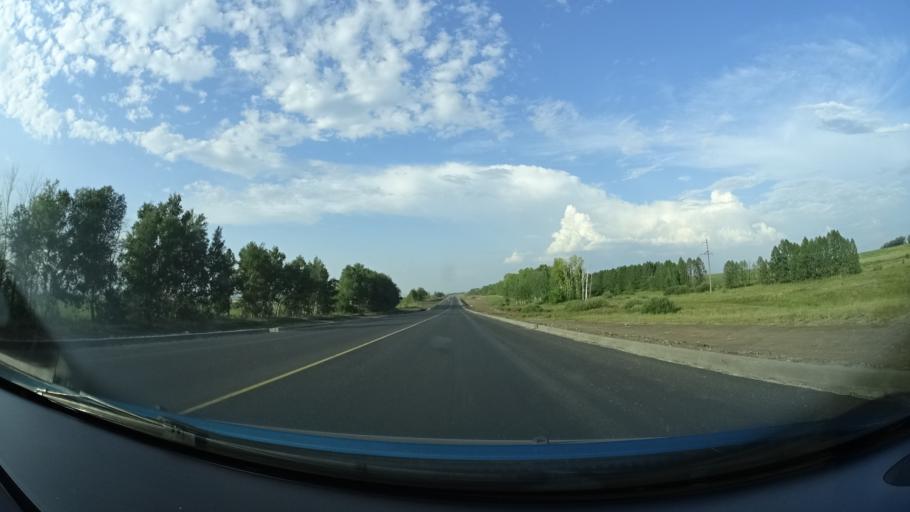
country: RU
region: Samara
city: Sukhodol
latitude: 53.7488
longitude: 50.8653
